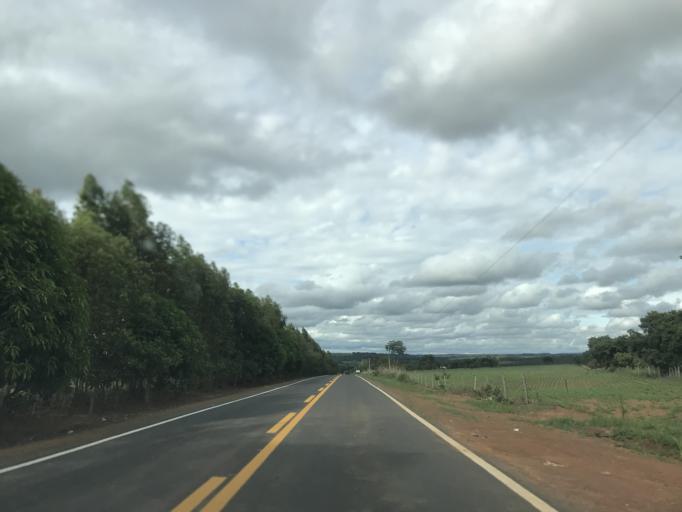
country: BR
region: Goias
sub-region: Bela Vista De Goias
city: Bela Vista de Goias
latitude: -17.1810
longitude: -48.6880
